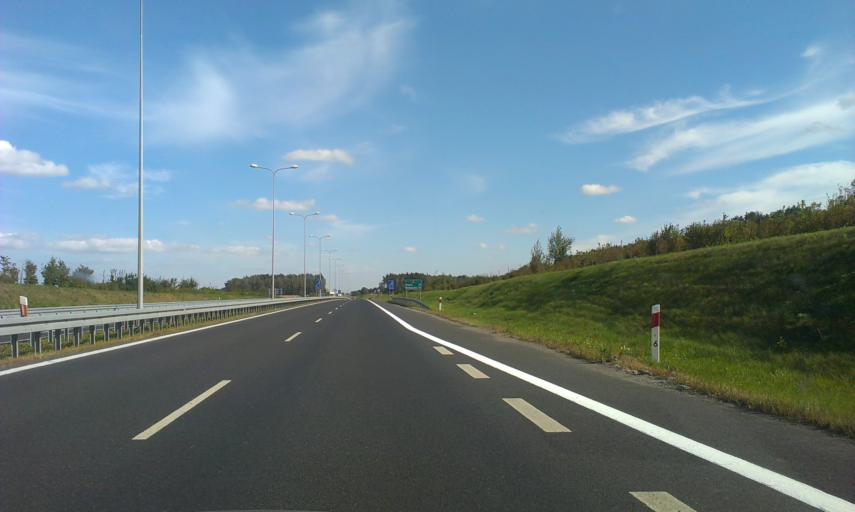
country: PL
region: Greater Poland Voivodeship
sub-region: Powiat pilski
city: Wyrzysk
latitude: 53.1628
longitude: 17.2271
